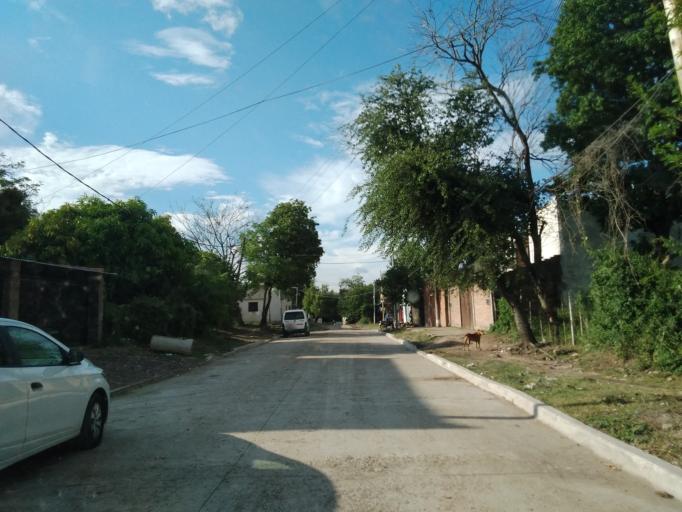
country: AR
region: Corrientes
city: Corrientes
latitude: -27.4599
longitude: -58.8163
